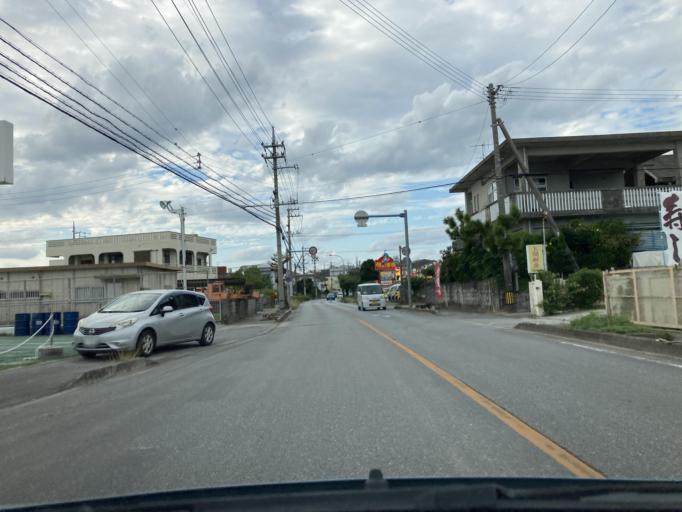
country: JP
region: Okinawa
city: Katsuren-haebaru
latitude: 26.3414
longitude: 127.8707
